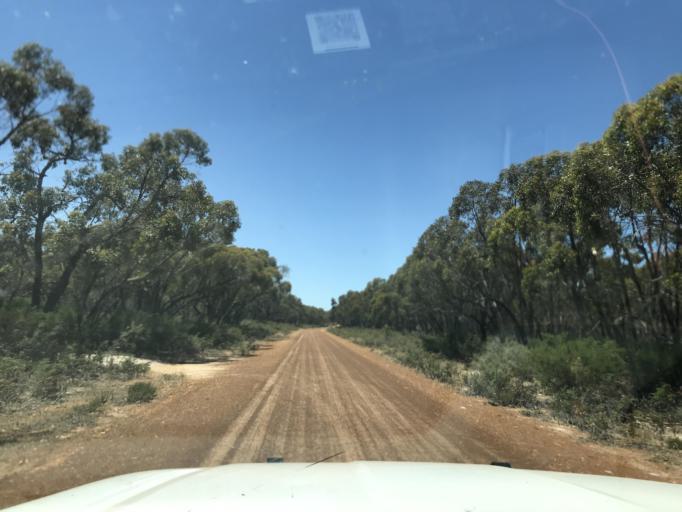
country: AU
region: South Australia
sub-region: Wattle Range
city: Penola
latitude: -37.0463
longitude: 141.3896
